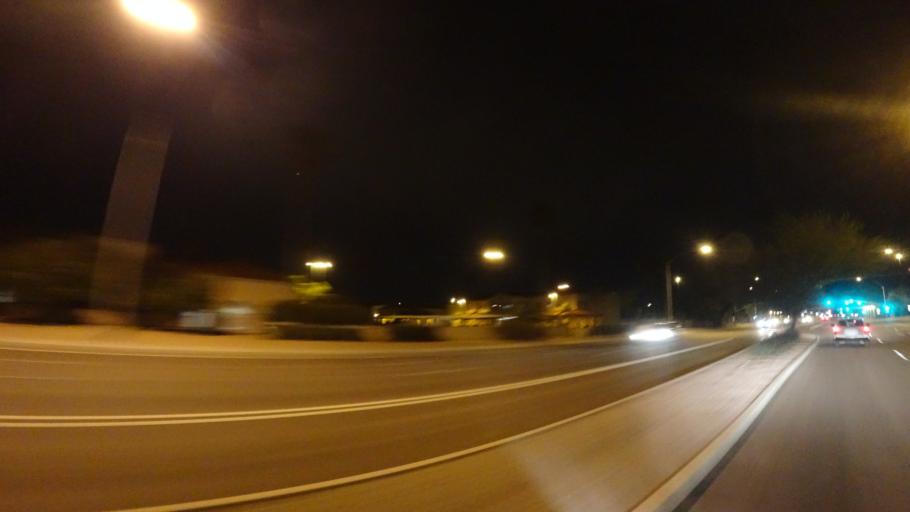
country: US
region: Arizona
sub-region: Maricopa County
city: Gilbert
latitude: 33.3887
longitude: -111.7367
